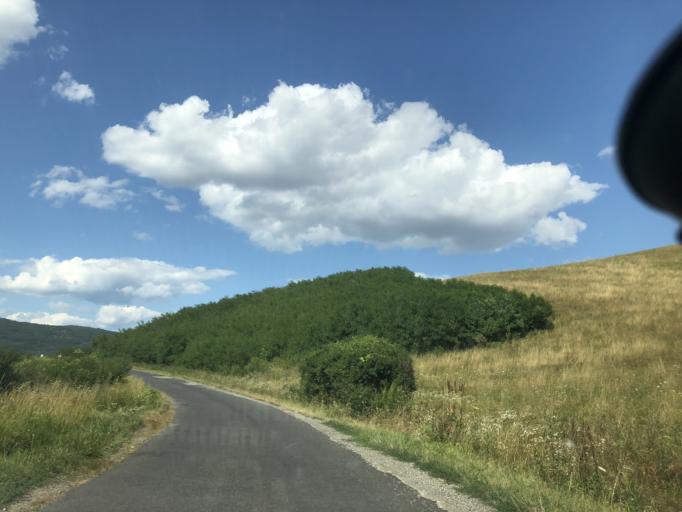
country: HU
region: Borsod-Abauj-Zemplen
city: Szendro
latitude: 48.5437
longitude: 20.7982
